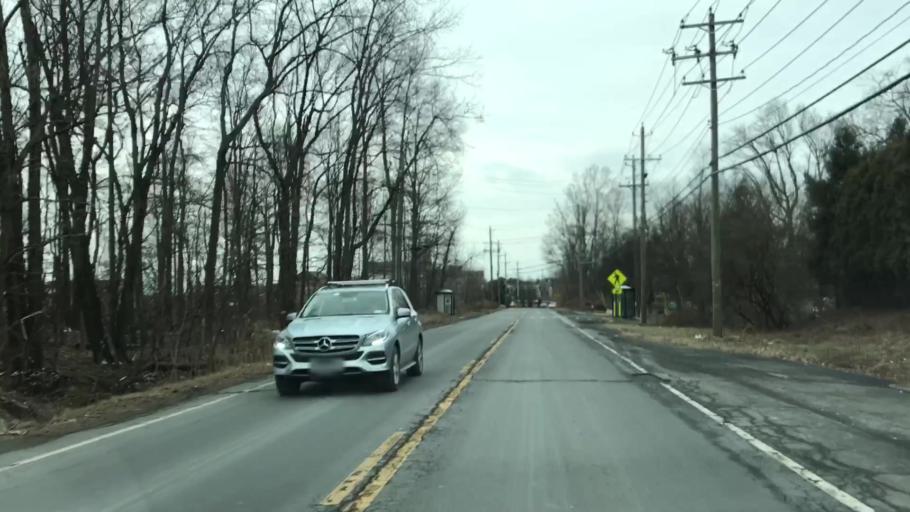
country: US
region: New York
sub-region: Rockland County
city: New Hempstead
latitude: 41.1450
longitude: -74.0343
